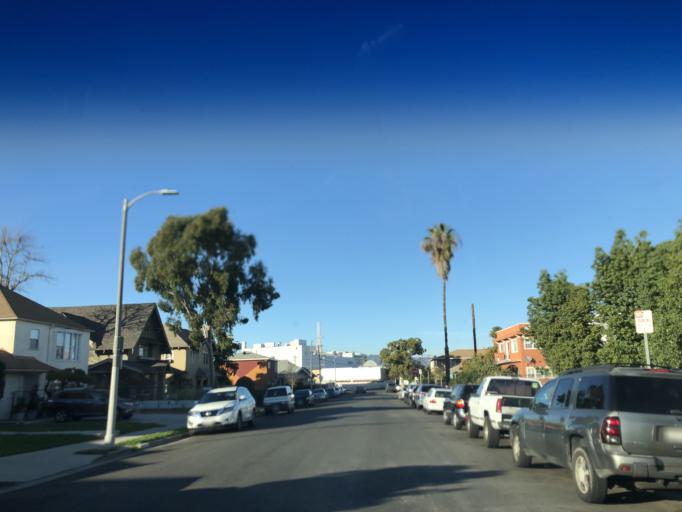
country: US
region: California
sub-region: Los Angeles County
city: Hollywood
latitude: 34.0447
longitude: -118.3237
